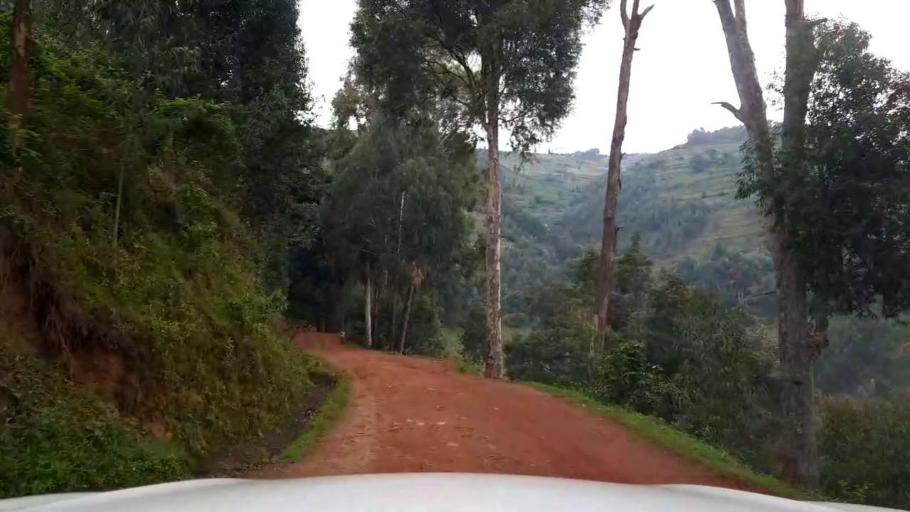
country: UG
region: Western Region
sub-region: Kisoro District
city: Kisoro
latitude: -1.3956
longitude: 29.8005
